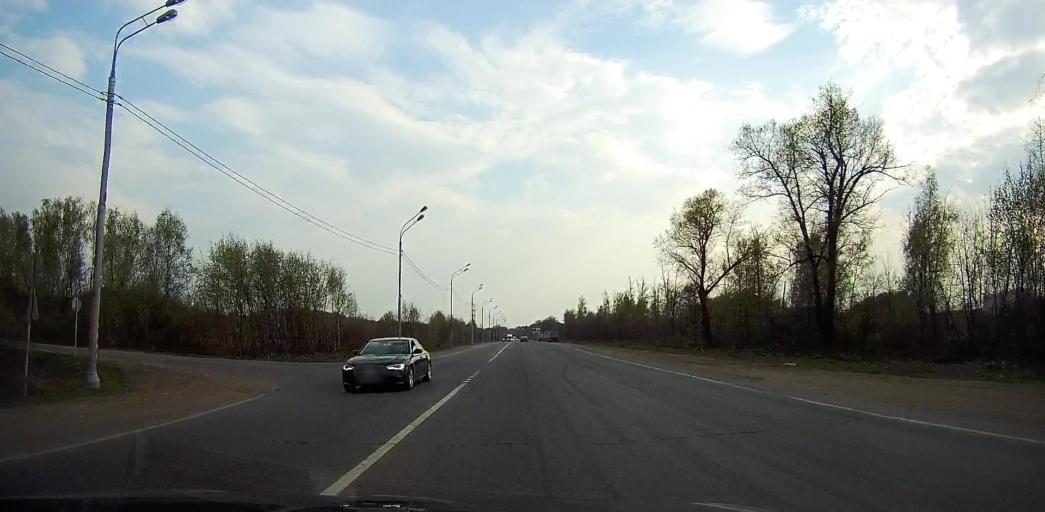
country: RU
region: Moskovskaya
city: Petrovskaya
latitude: 55.5409
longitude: 37.7716
